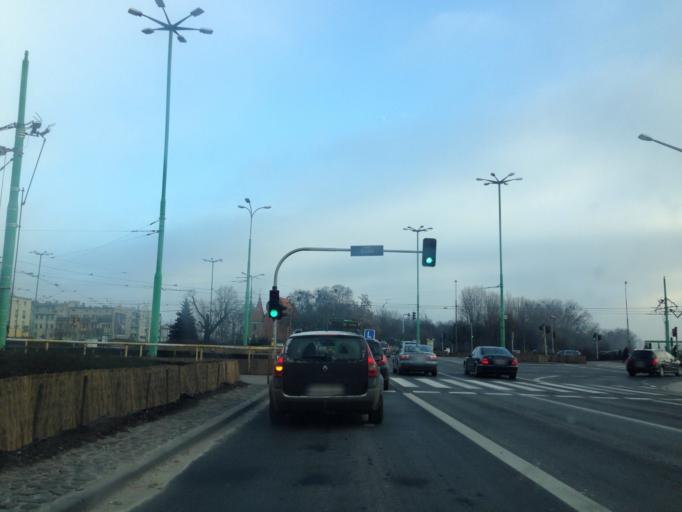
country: PL
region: Greater Poland Voivodeship
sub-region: Poznan
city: Poznan
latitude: 52.4101
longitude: 16.9557
